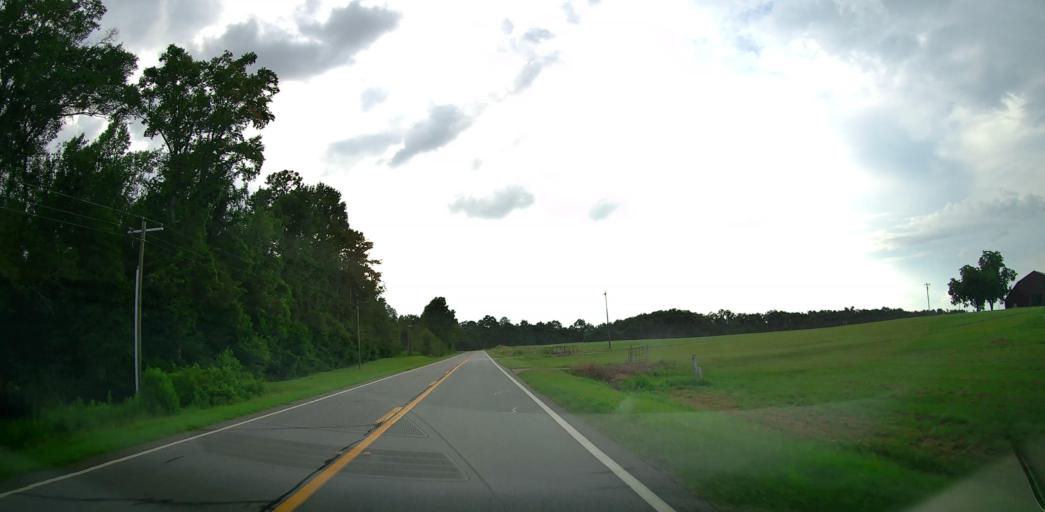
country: US
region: Georgia
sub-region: Pulaski County
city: Hawkinsville
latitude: 32.2942
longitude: -83.5188
